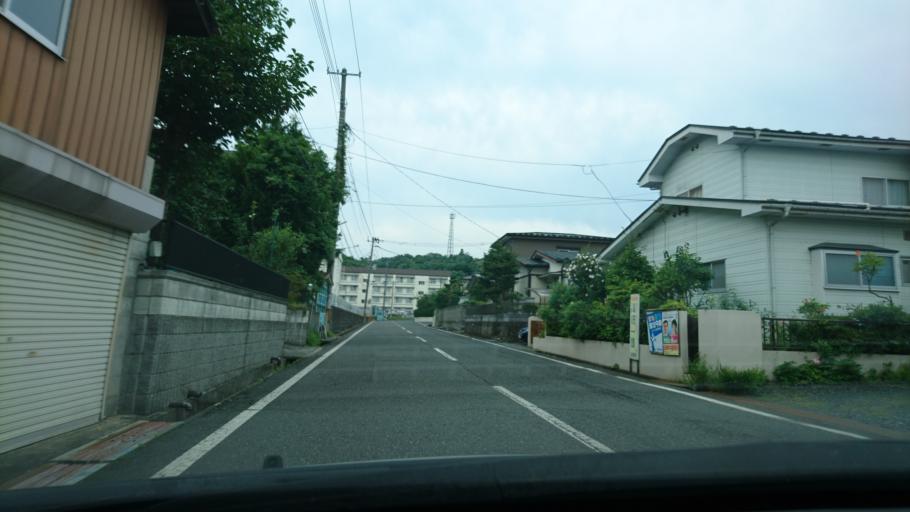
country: JP
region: Iwate
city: Ichinoseki
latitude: 38.9156
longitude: 141.1488
